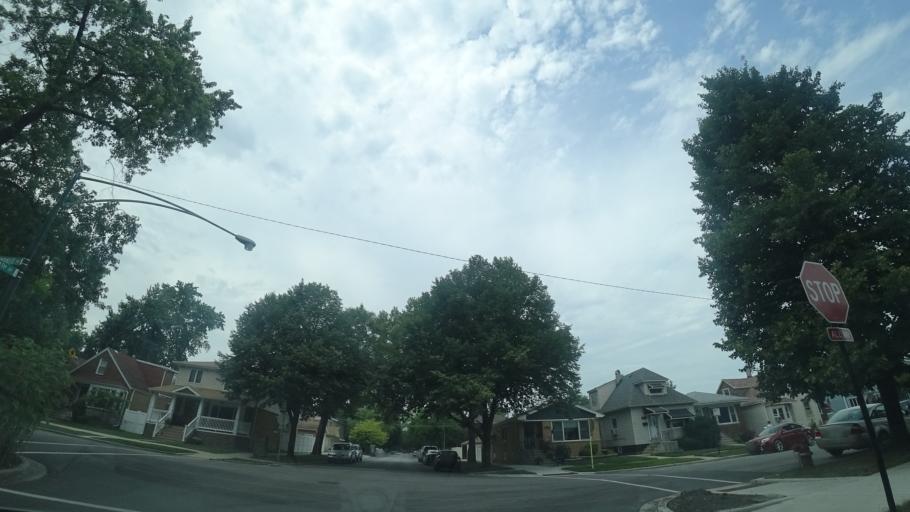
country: US
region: Illinois
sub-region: Cook County
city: Merrionette Park
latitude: 41.6932
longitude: -87.7130
